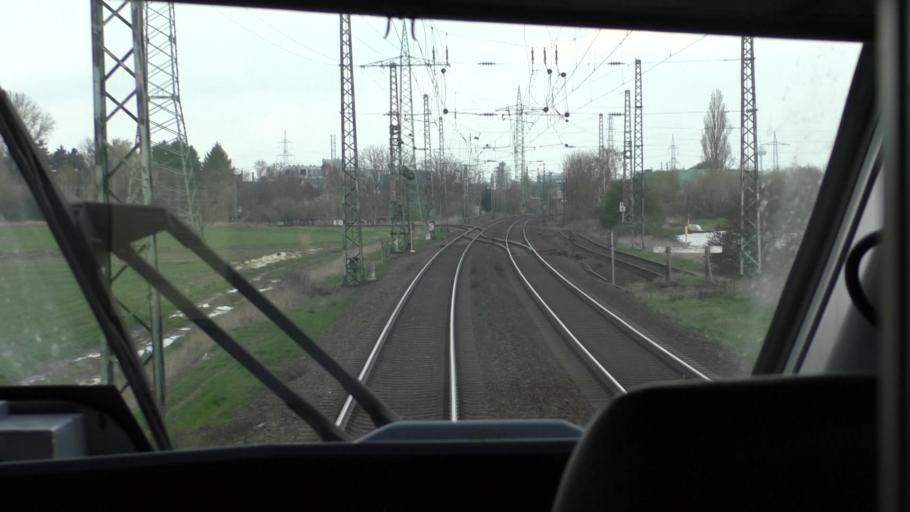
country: DE
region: North Rhine-Westphalia
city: Bruhl
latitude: 50.8680
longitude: 6.9086
